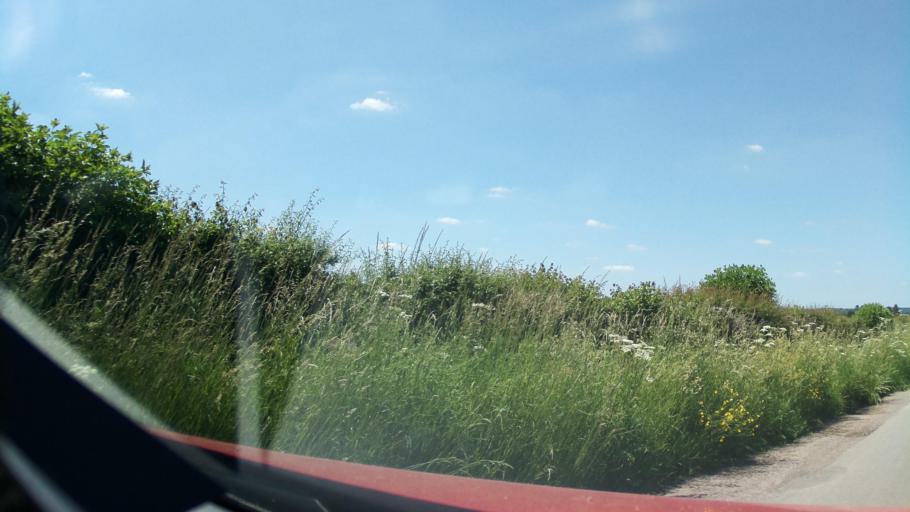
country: GB
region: England
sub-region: Wiltshire
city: Bremhill
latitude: 51.4492
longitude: -2.0611
